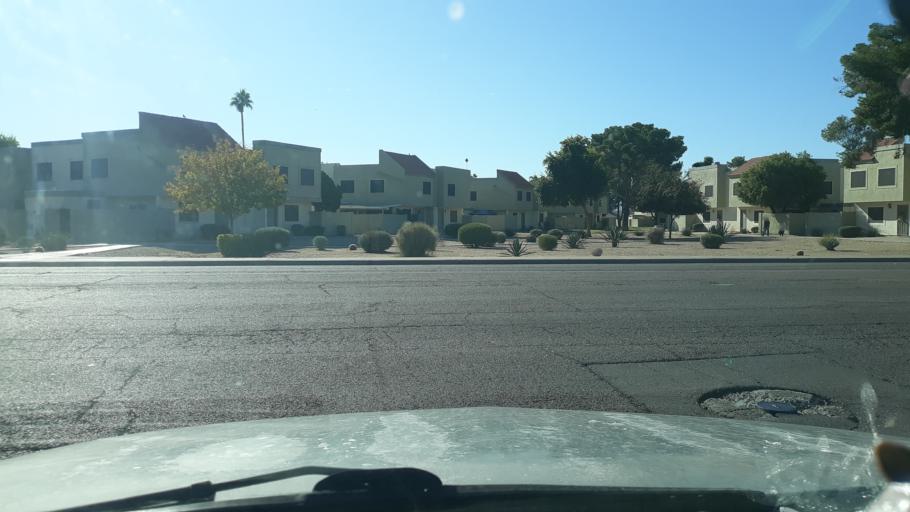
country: US
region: Arizona
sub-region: Maricopa County
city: Glendale
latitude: 33.5241
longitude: -112.1620
